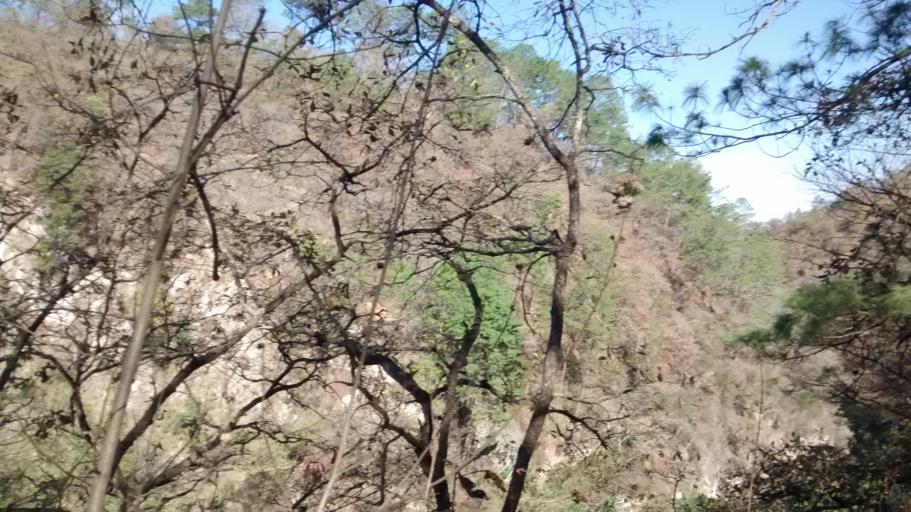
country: GT
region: Sacatepequez
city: Santo Domingo Xenacoj
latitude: 14.6786
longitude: -90.7218
